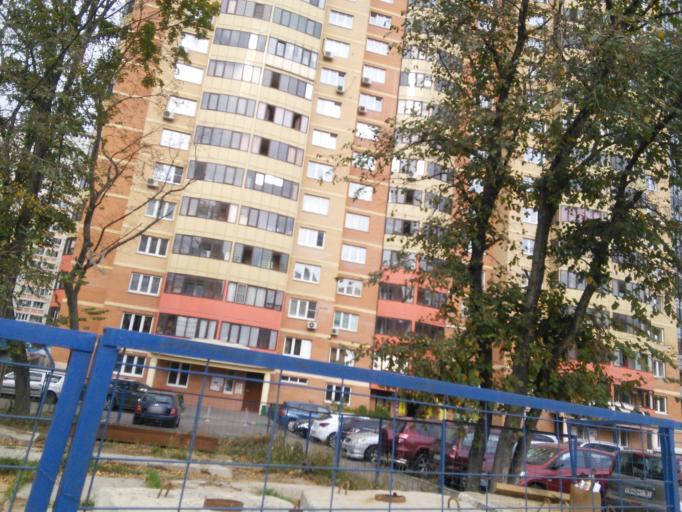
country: RU
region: Moskovskaya
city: Levoberezhnyy
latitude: 55.8650
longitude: 37.4737
